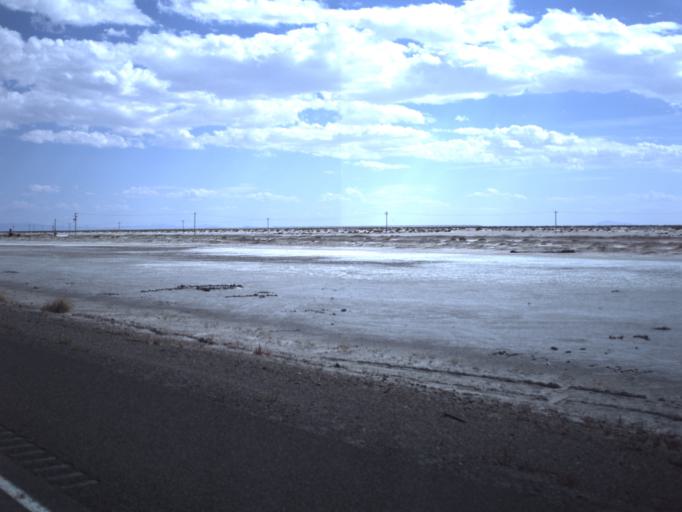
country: US
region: Utah
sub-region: Tooele County
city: Wendover
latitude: 40.7378
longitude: -113.8199
